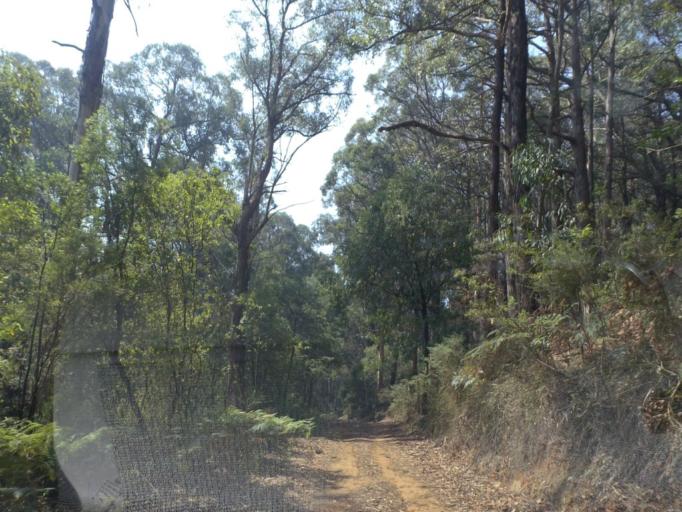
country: AU
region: Victoria
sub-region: Yarra Ranges
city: Healesville
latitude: -37.5637
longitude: 145.6215
